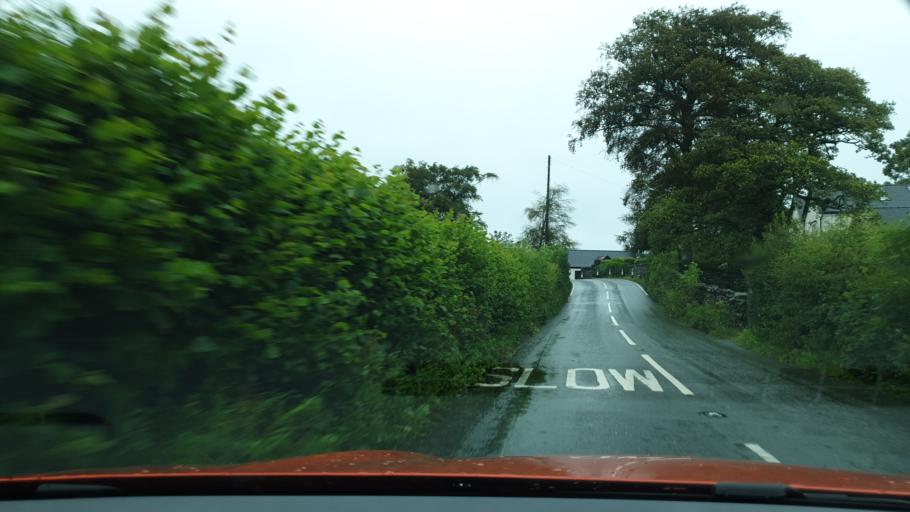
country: GB
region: England
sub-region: Cumbria
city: Ulverston
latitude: 54.2894
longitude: -3.0933
